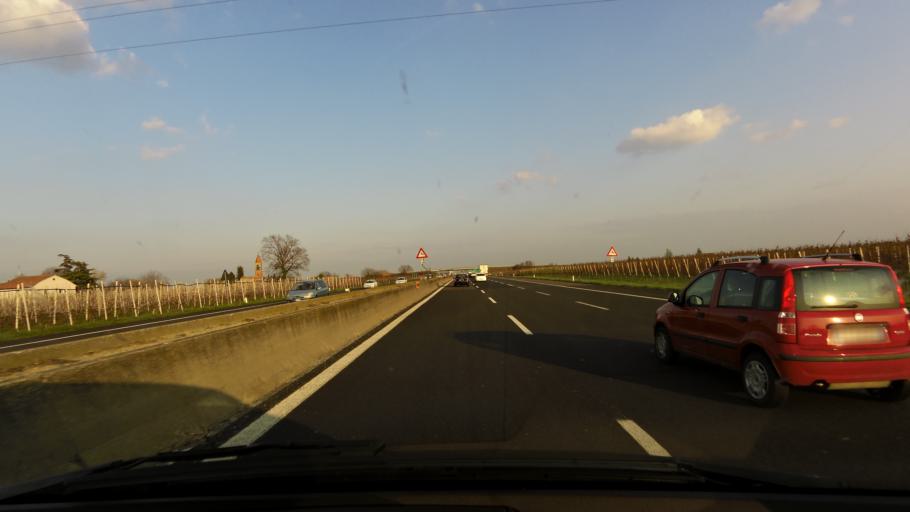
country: IT
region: Emilia-Romagna
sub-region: Provincia di Bologna
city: Mordano
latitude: 44.3605
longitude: 11.7944
